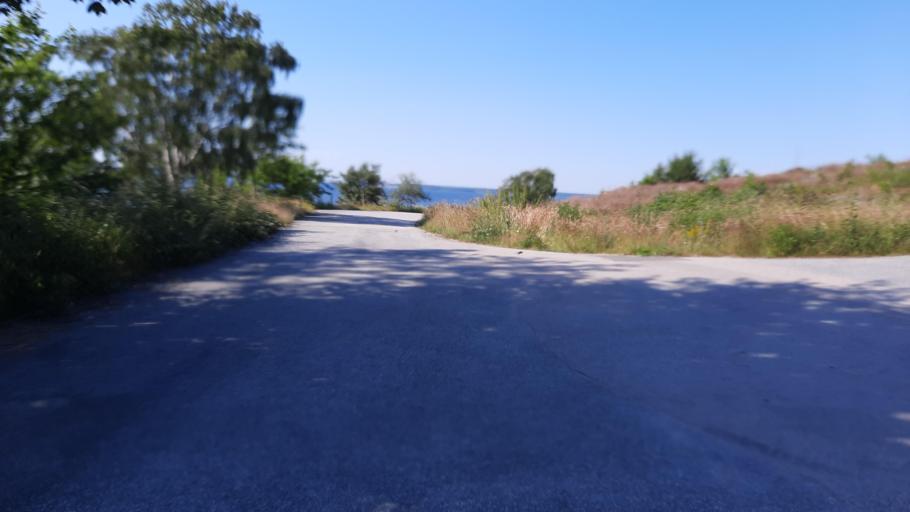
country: SE
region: Blekinge
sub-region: Karlskrona Kommun
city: Sturko
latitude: 56.1208
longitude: 15.6518
